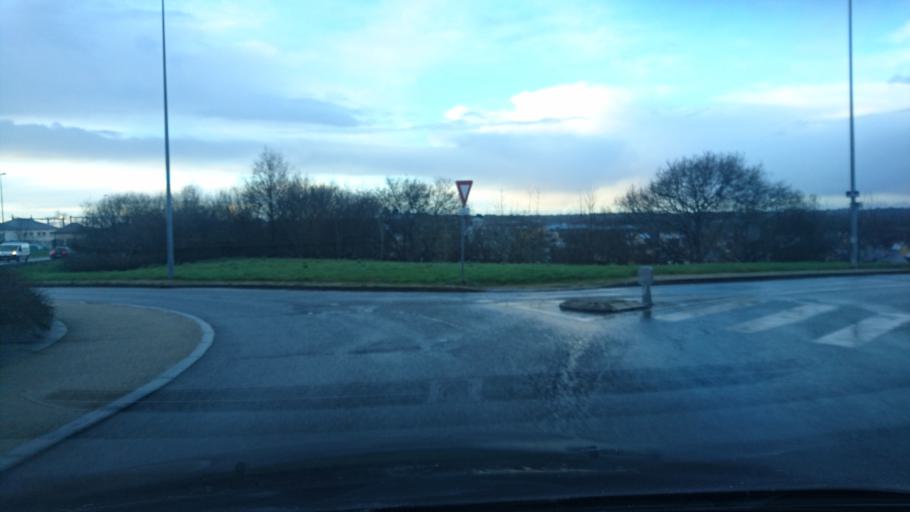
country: FR
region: Brittany
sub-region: Departement du Finistere
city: Guilers
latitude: 48.3907
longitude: -4.5373
